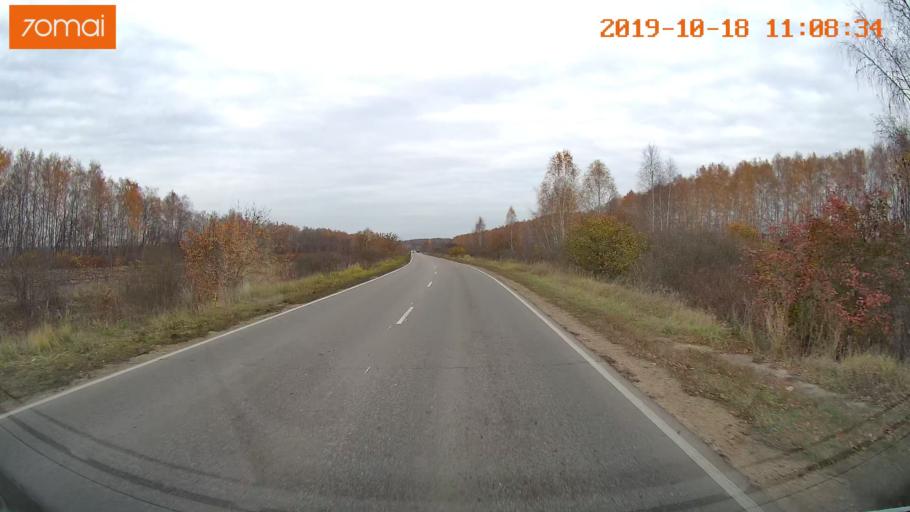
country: RU
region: Tula
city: Kimovsk
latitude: 53.9401
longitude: 38.5366
